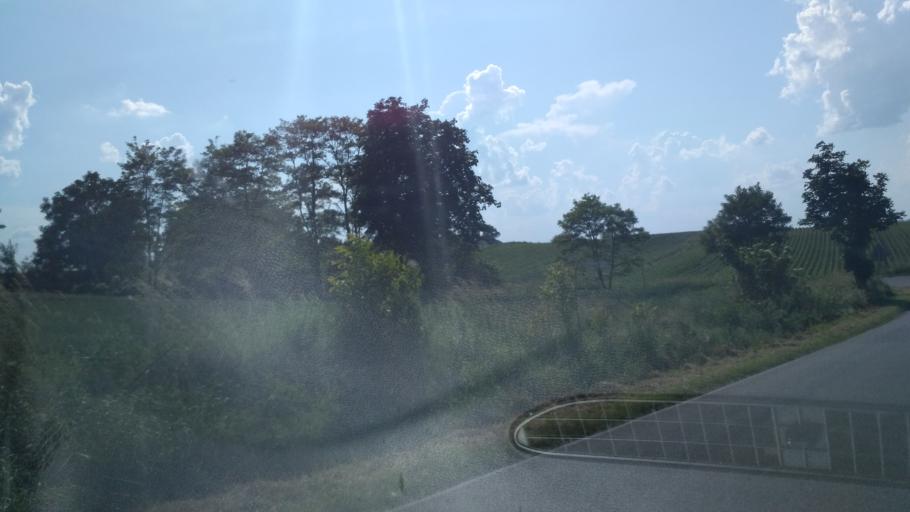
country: PL
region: Subcarpathian Voivodeship
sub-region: Powiat jaroslawski
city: Rokietnica
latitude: 49.9348
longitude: 22.6667
